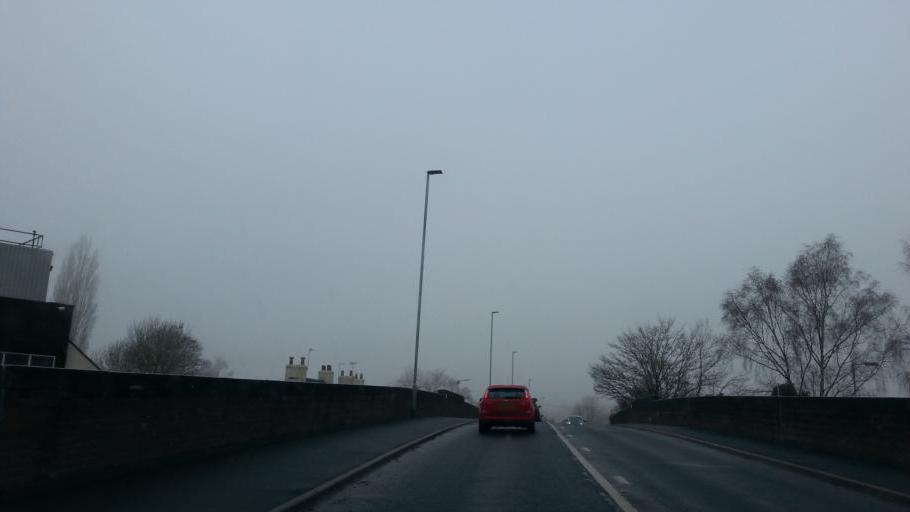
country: GB
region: England
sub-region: Cheshire East
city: Congleton
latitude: 53.1572
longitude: -2.1925
